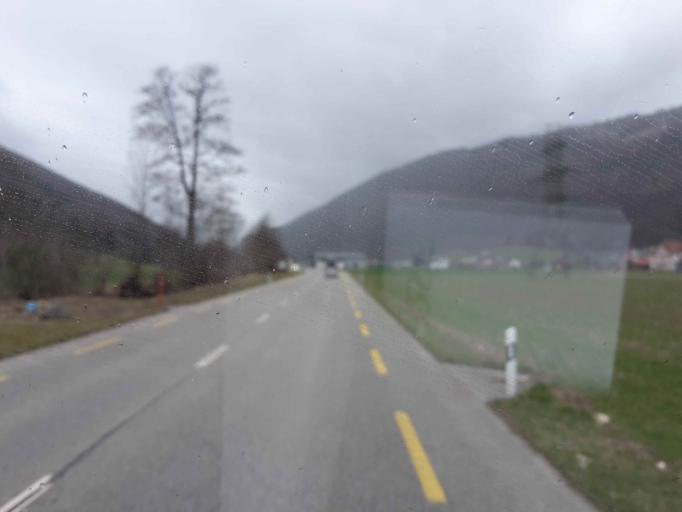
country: CH
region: Solothurn
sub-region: Bezirk Thal
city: Matzendorf
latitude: 47.2945
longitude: 7.5993
